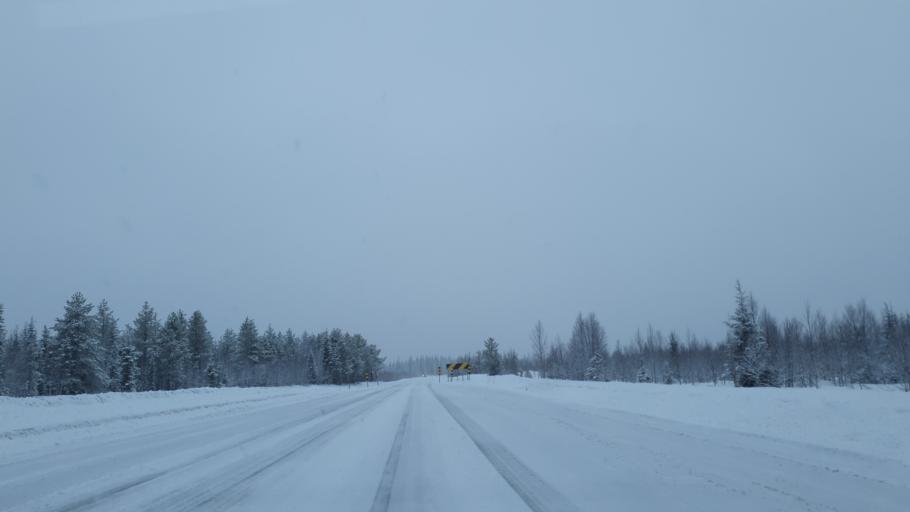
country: FI
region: Lapland
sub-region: Tunturi-Lappi
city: Kittilae
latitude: 67.6328
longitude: 24.5897
